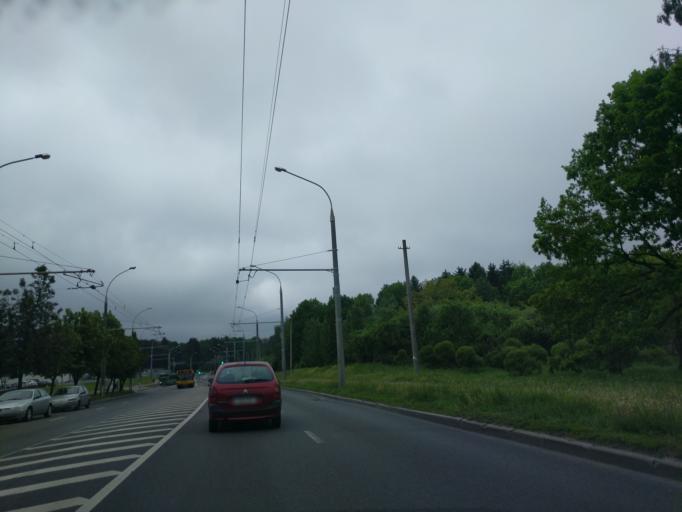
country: BY
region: Minsk
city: Novoye Medvezhino
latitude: 53.8912
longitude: 27.4392
